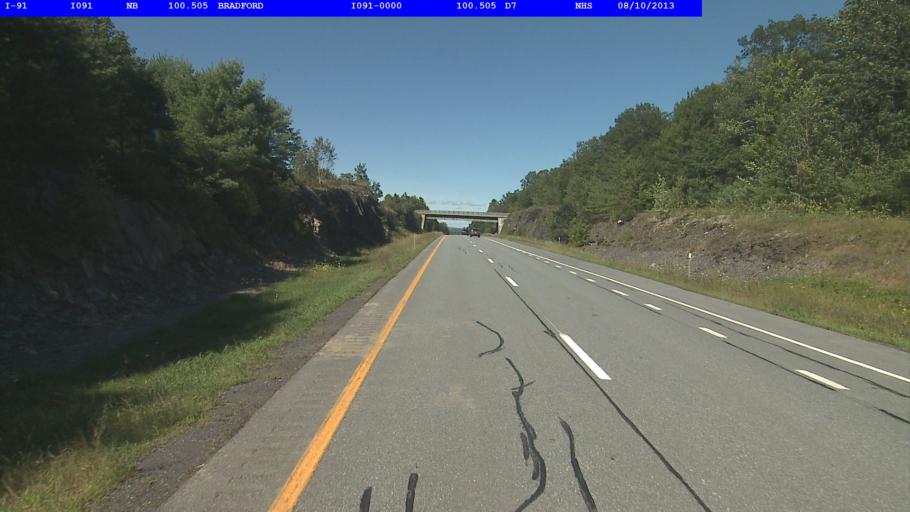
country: US
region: New Hampshire
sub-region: Grafton County
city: Haverhill
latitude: 44.0219
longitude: -72.1175
